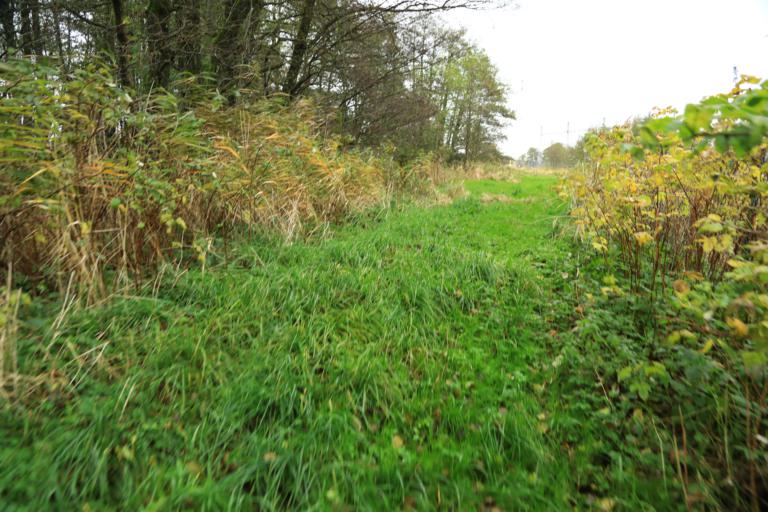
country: SE
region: Halland
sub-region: Varbergs Kommun
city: Varberg
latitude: 57.1278
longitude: 12.3002
